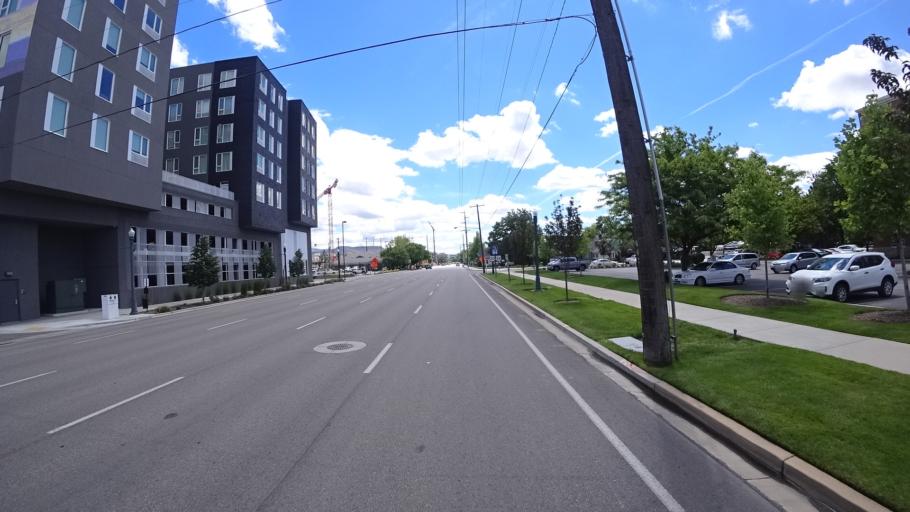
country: US
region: Idaho
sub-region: Ada County
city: Boise
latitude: 43.6114
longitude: -116.2035
